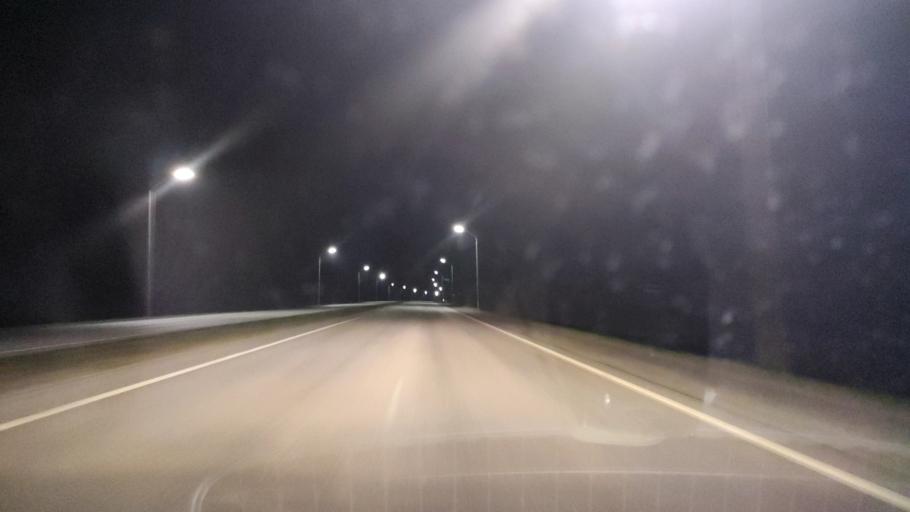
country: RU
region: Belgorod
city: Staryy Oskol
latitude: 51.3765
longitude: 37.8506
